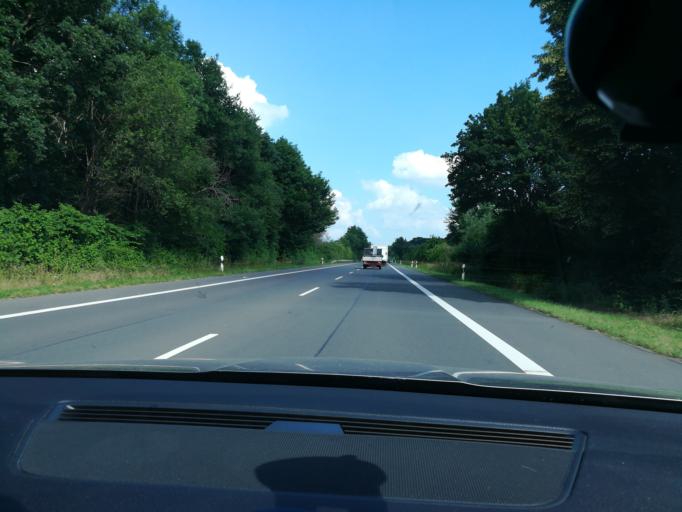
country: DE
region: North Rhine-Westphalia
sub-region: Regierungsbezirk Detmold
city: Petershagen
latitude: 52.3831
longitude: 8.8970
